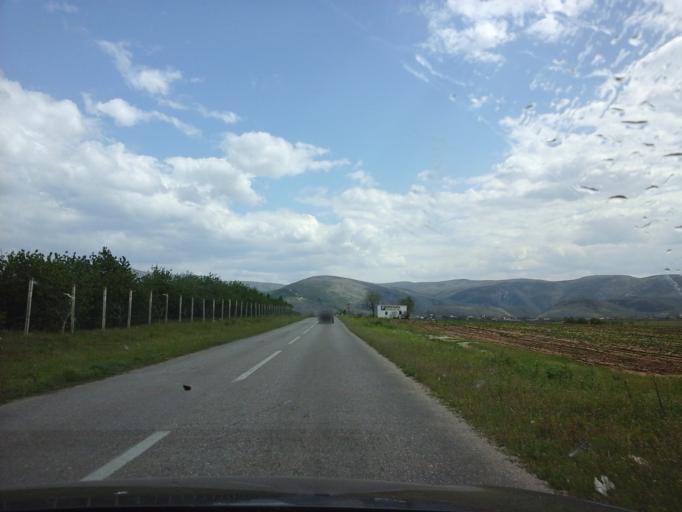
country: BA
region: Federation of Bosnia and Herzegovina
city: Blagaj
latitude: 43.2734
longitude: 17.8576
